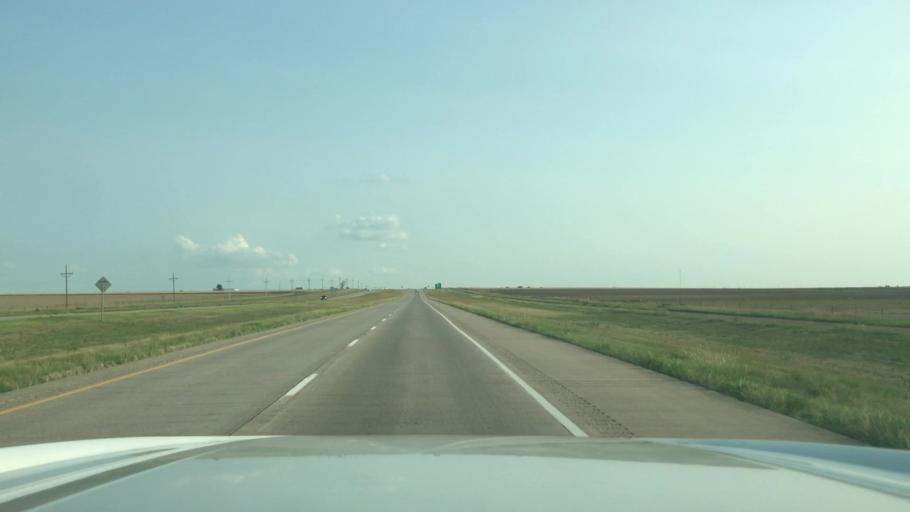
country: US
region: Texas
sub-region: Randall County
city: Canyon
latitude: 34.8279
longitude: -101.8489
